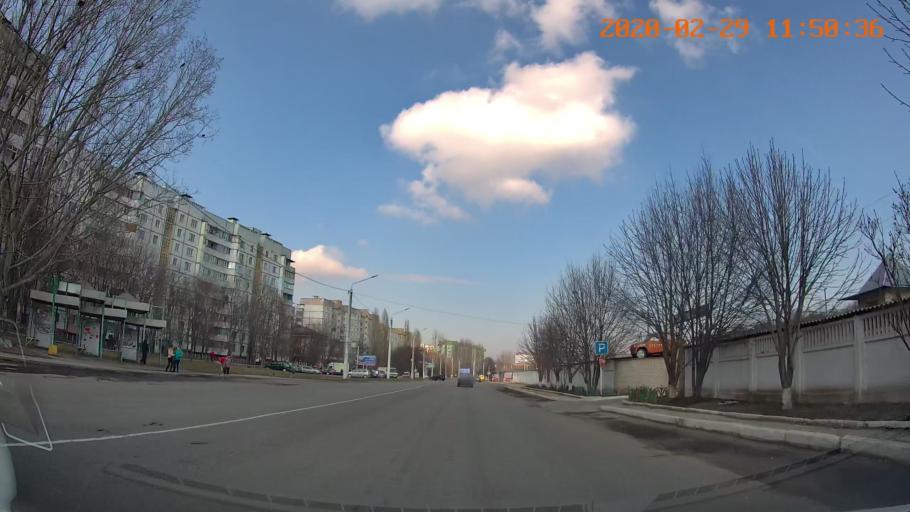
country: MD
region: Telenesti
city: Ribnita
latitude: 47.7591
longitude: 28.9904
